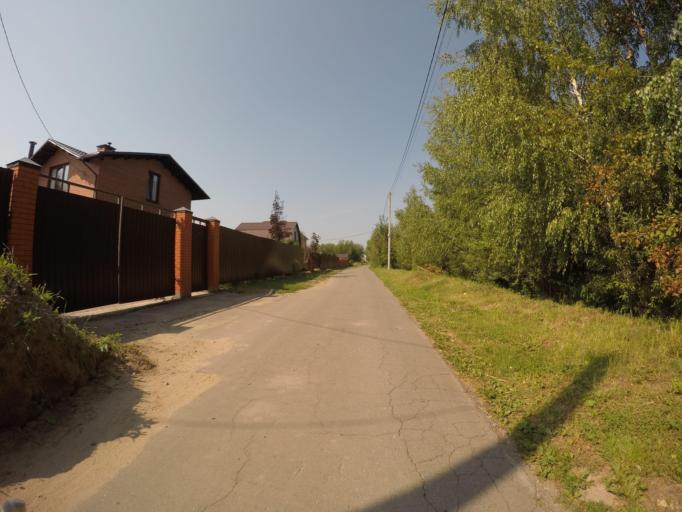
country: RU
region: Moskovskaya
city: Rechitsy
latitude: 55.6124
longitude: 38.5428
